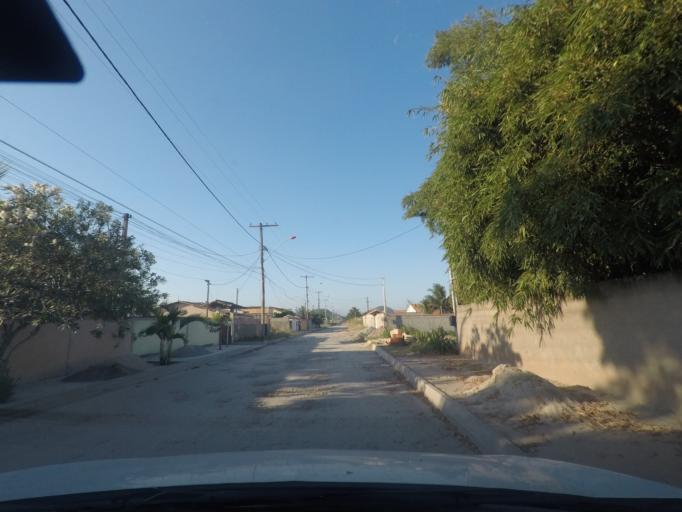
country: BR
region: Rio de Janeiro
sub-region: Marica
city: Marica
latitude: -22.9655
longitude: -42.9334
